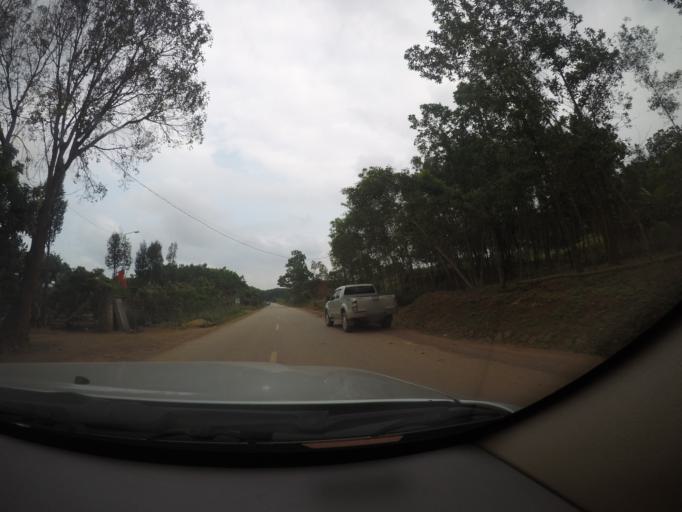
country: VN
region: Quang Binh
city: Kien Giang
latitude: 17.1380
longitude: 106.7683
